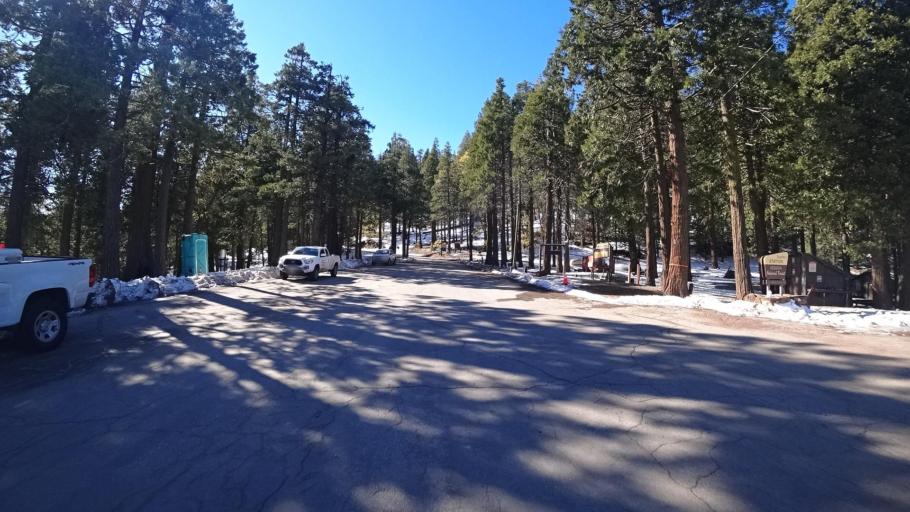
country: US
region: California
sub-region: Kern County
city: Alta Sierra
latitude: 35.7381
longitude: -118.5567
